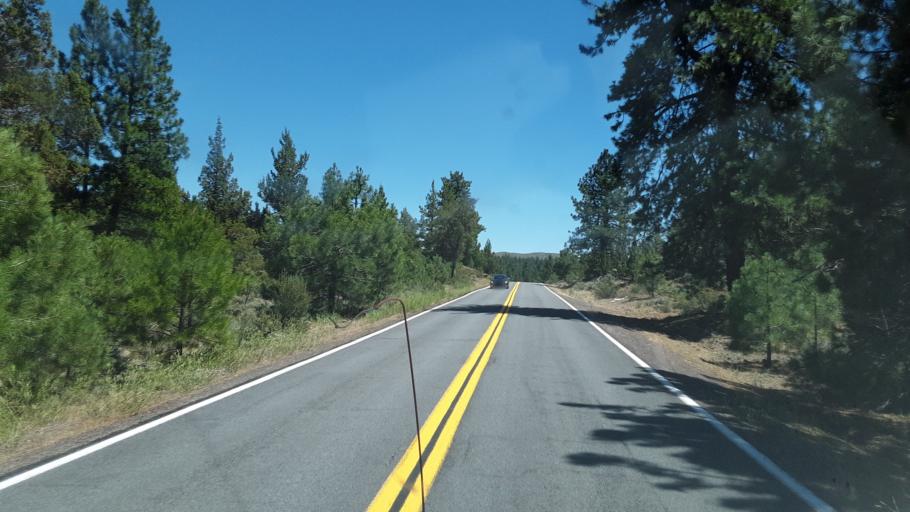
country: US
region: California
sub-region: Lassen County
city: Susanville
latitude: 40.6338
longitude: -120.6492
